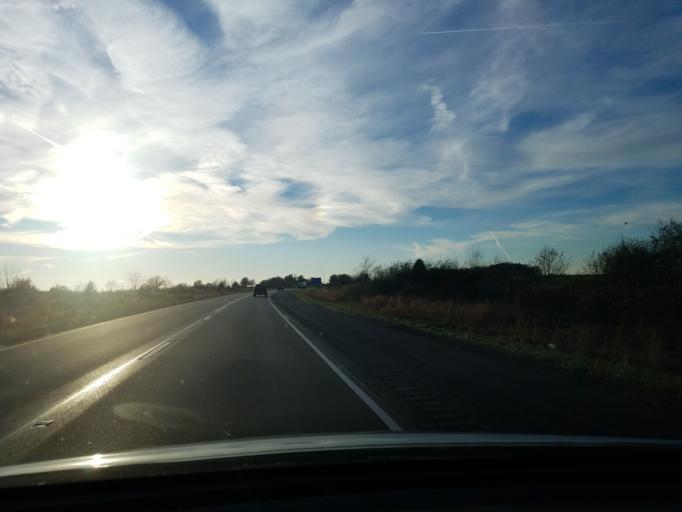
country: US
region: Indiana
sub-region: Spencer County
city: Dale
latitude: 38.1971
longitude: -86.9385
